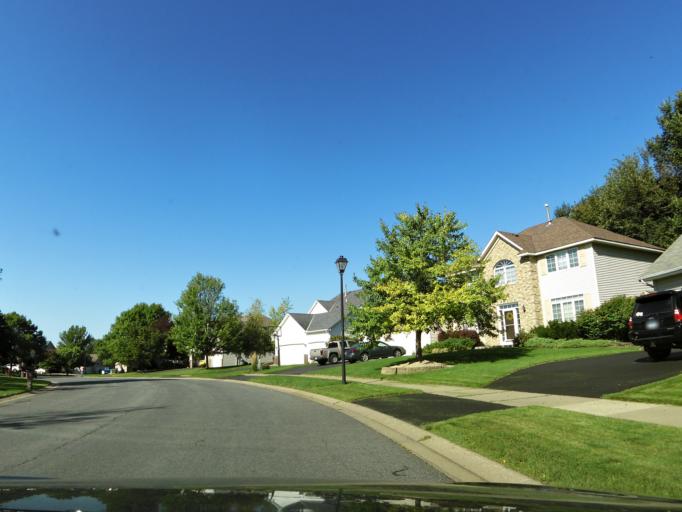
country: US
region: Minnesota
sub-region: Scott County
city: Savage
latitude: 44.7337
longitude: -93.3492
